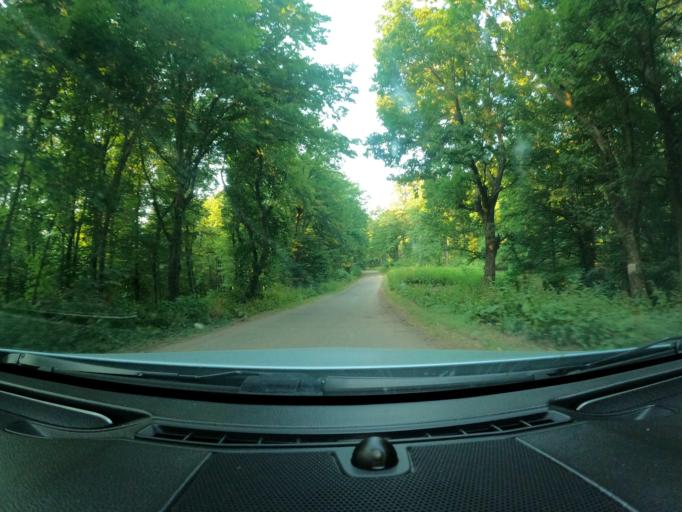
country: RS
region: Autonomna Pokrajina Vojvodina
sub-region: Juznobacki Okrug
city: Beocin
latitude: 45.1552
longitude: 19.7319
